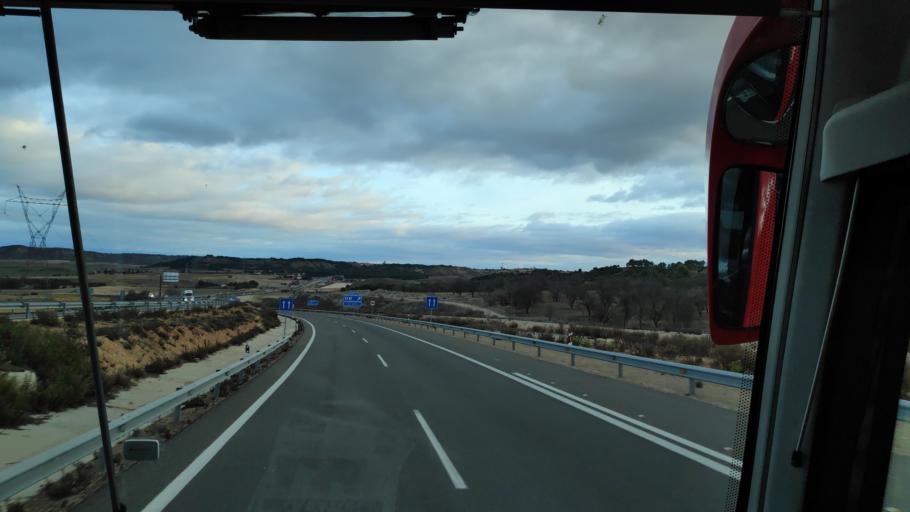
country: ES
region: Castille-La Mancha
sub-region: Provincia de Cuenca
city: Belinchon
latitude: 40.0448
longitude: -3.0614
